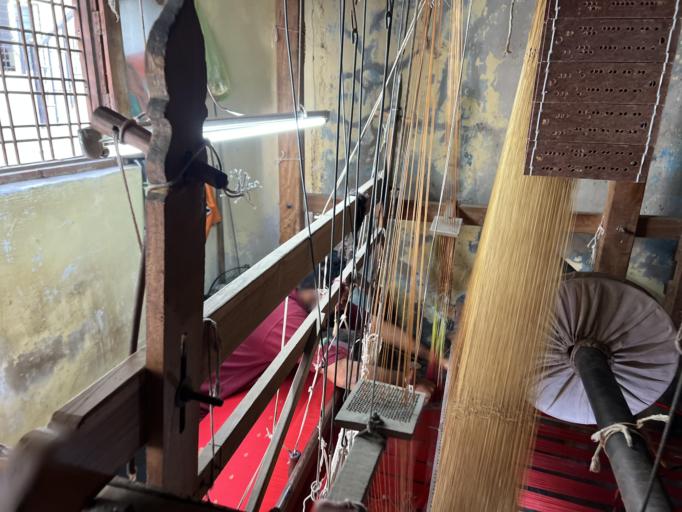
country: IN
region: Maharashtra
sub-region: Nashik Division
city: Yeola
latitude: 20.0407
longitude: 74.4883
